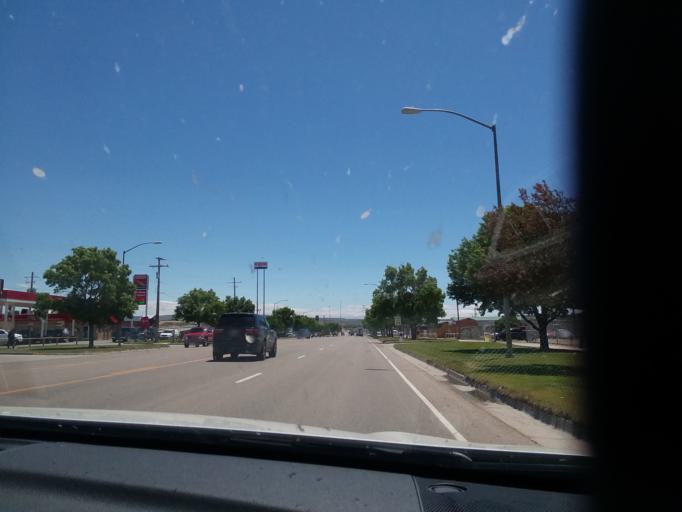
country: US
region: Wyoming
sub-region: Sweetwater County
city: Rock Springs
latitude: 41.6153
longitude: -109.2316
